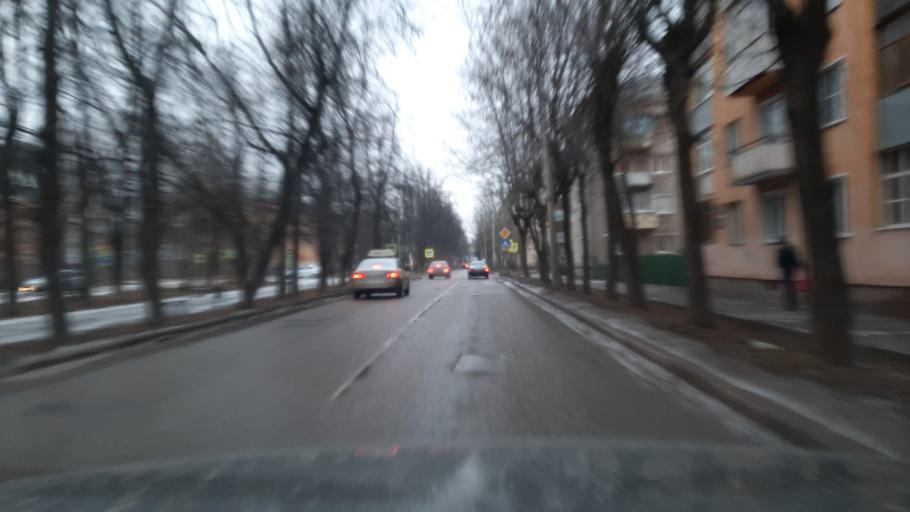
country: RU
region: Ivanovo
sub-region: Gorod Ivanovo
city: Ivanovo
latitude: 56.9988
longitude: 40.9902
